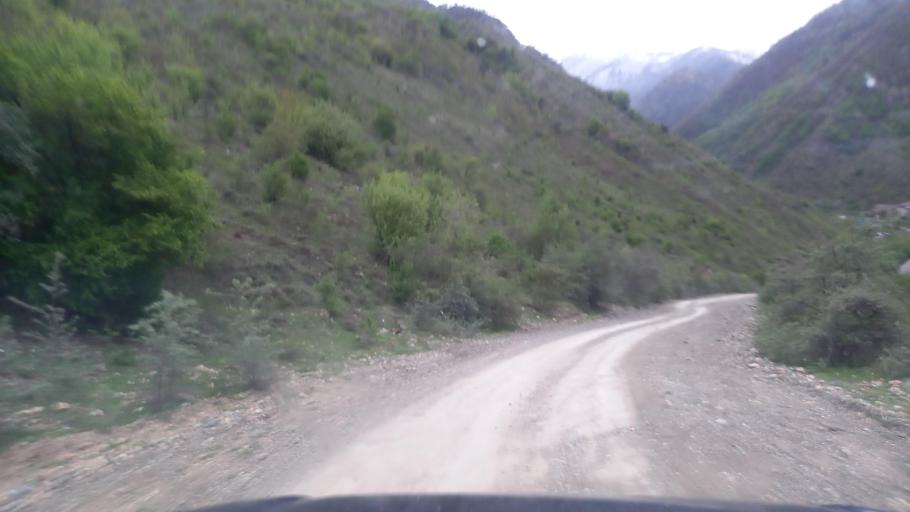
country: RU
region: North Ossetia
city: Mizur
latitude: 42.8533
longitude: 44.1586
